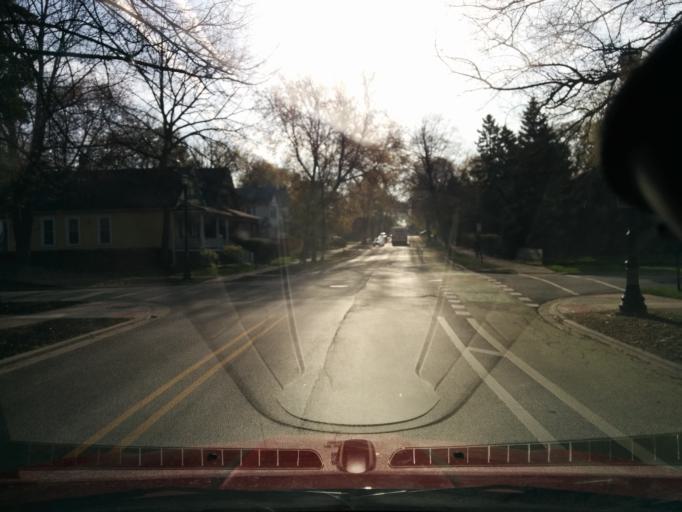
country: US
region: Illinois
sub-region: Cook County
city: Evanston
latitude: 42.0486
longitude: -87.6940
